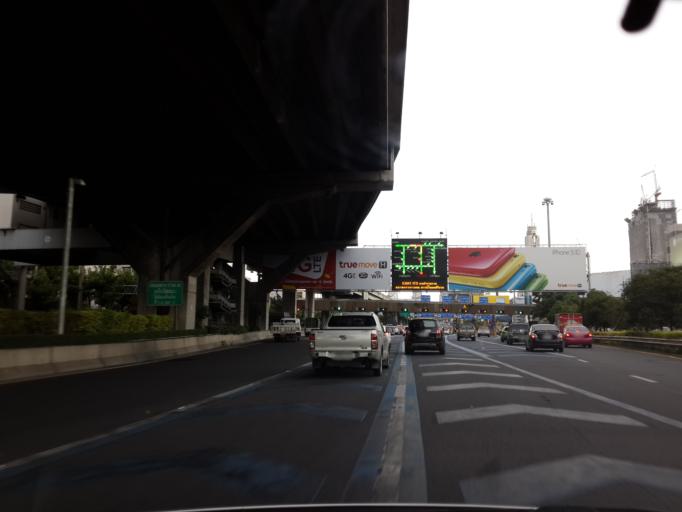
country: TH
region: Bangkok
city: Din Daeng
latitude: 13.7683
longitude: 100.5504
